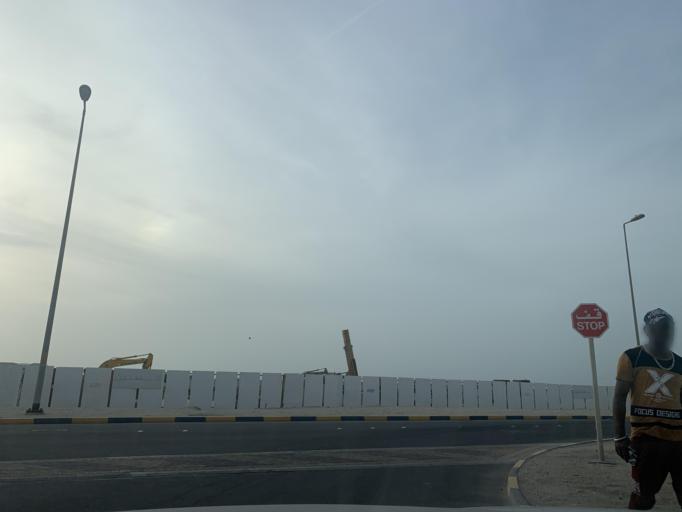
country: BH
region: Muharraq
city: Al Muharraq
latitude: 26.3104
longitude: 50.6186
